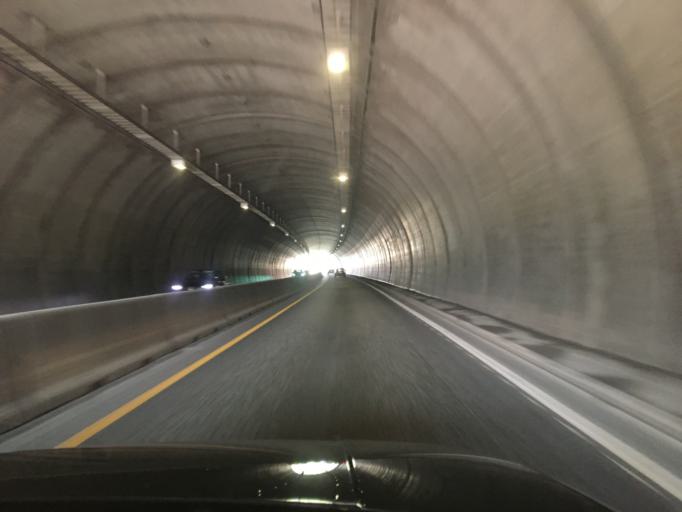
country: NO
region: Telemark
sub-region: Porsgrunn
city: Porsgrunn
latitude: 59.0807
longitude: 9.6654
